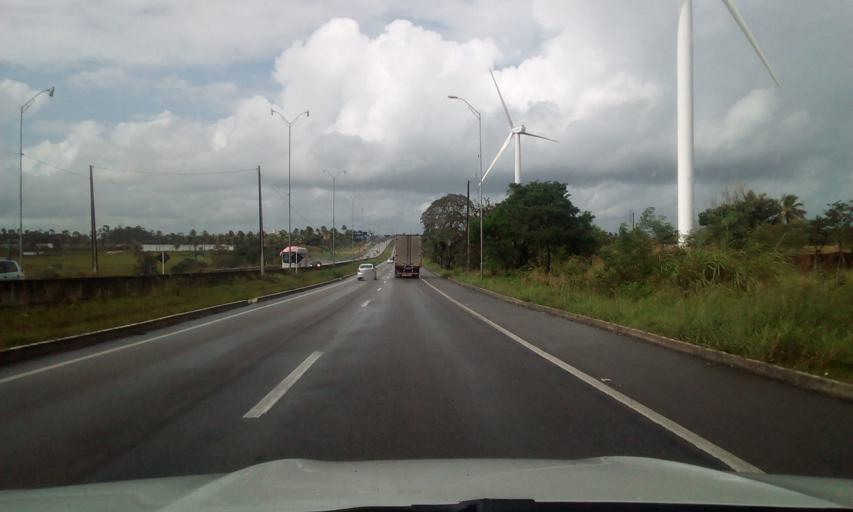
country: BR
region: Paraiba
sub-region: Conde
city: Conde
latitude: -7.2648
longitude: -34.9369
